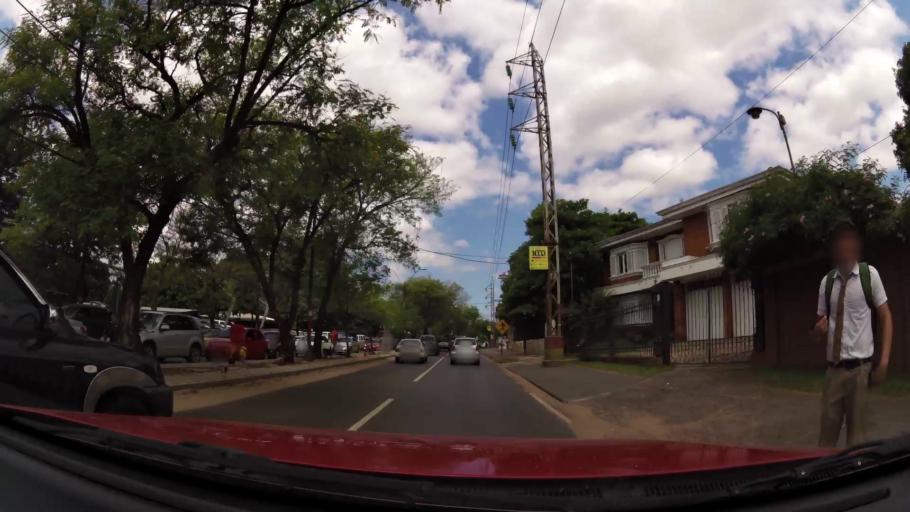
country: PY
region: Central
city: Fernando de la Mora
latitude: -25.3044
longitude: -57.5370
